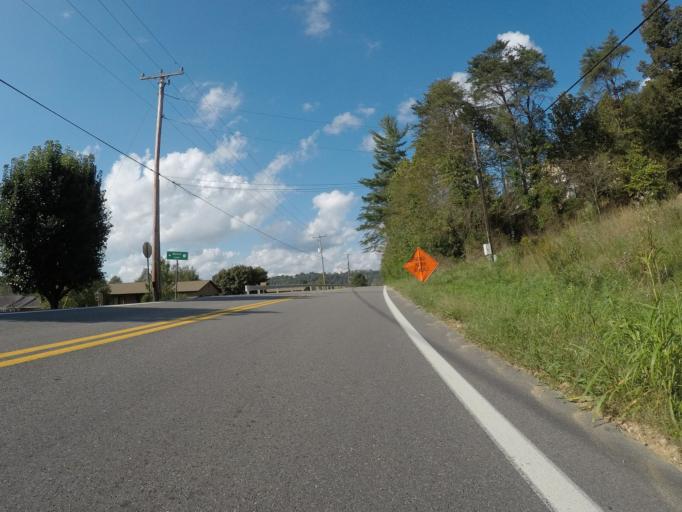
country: US
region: Ohio
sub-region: Lawrence County
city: Burlington
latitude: 38.3610
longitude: -82.5149
